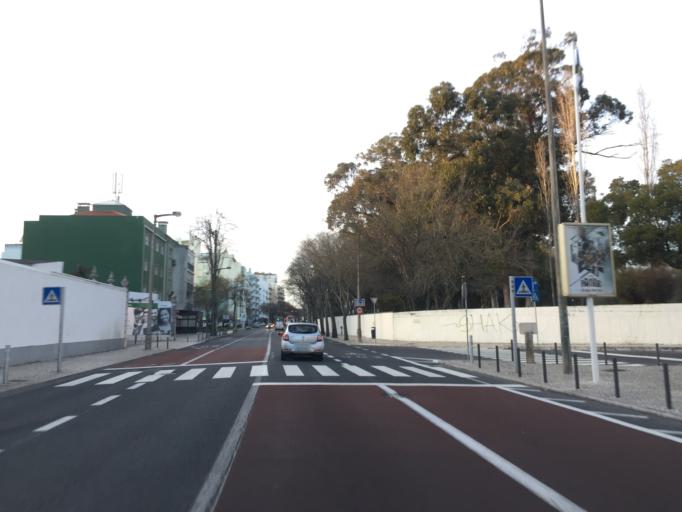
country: PT
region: Lisbon
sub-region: Odivelas
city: Olival do Basto
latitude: 38.7685
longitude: -9.1586
